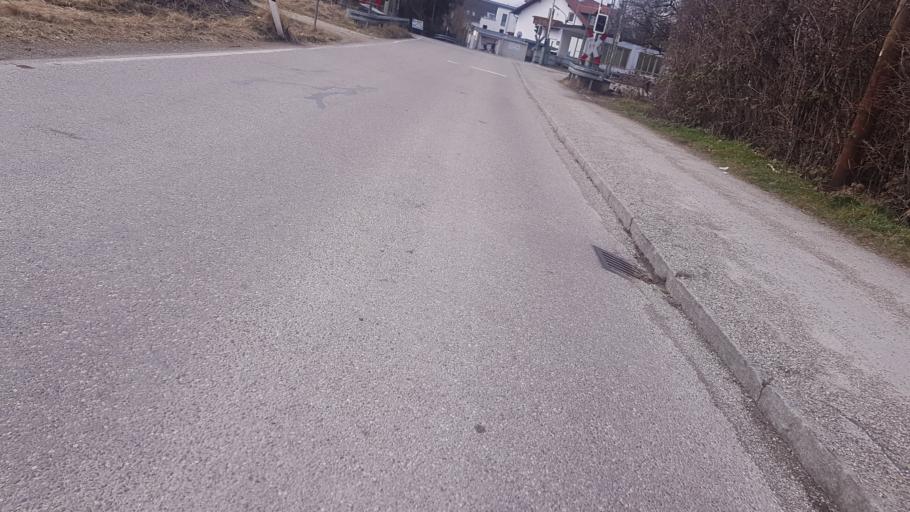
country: DE
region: Bavaria
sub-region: Upper Bavaria
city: Bogenhausen
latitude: 48.1561
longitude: 11.6489
